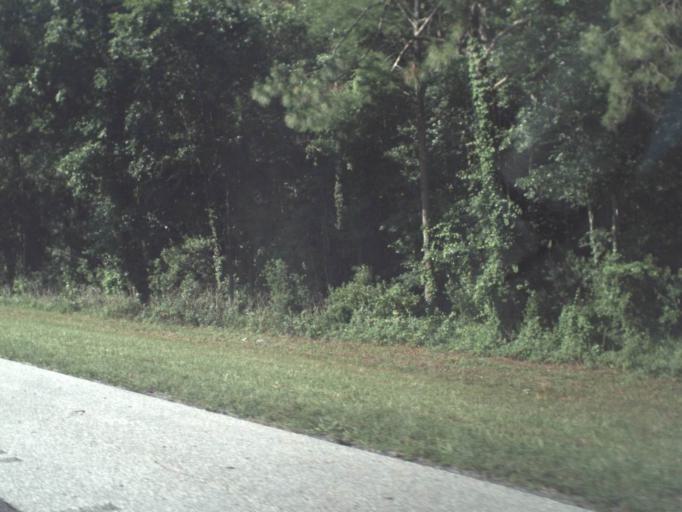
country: US
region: Florida
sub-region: Saint Johns County
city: Saint Augustine Shores
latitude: 29.7911
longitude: -81.3637
